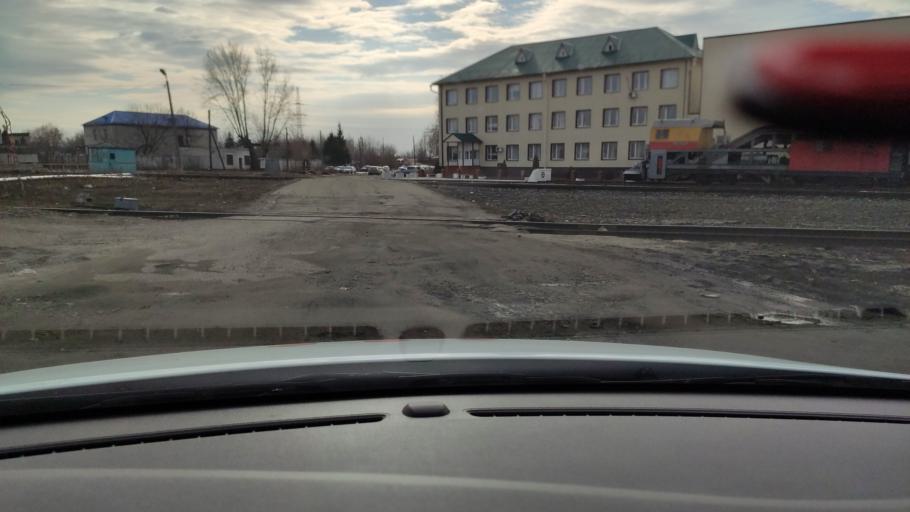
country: RU
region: Tatarstan
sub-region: Gorod Kazan'
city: Kazan
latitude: 55.7836
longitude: 49.1006
